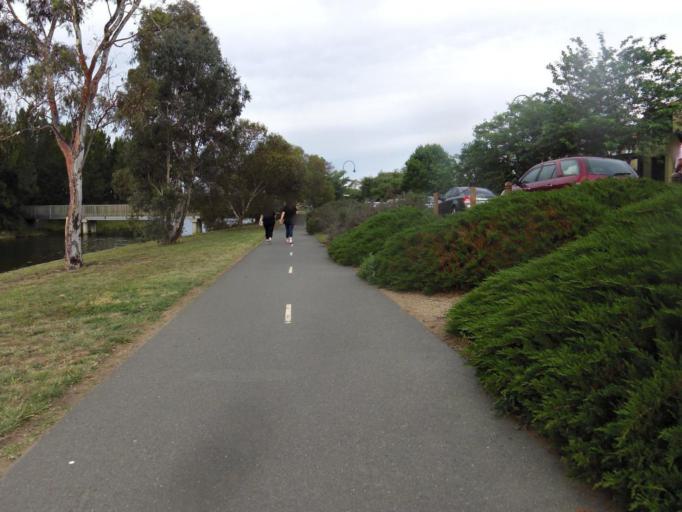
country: AU
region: Australian Capital Territory
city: Kaleen
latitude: -35.1754
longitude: 149.1355
